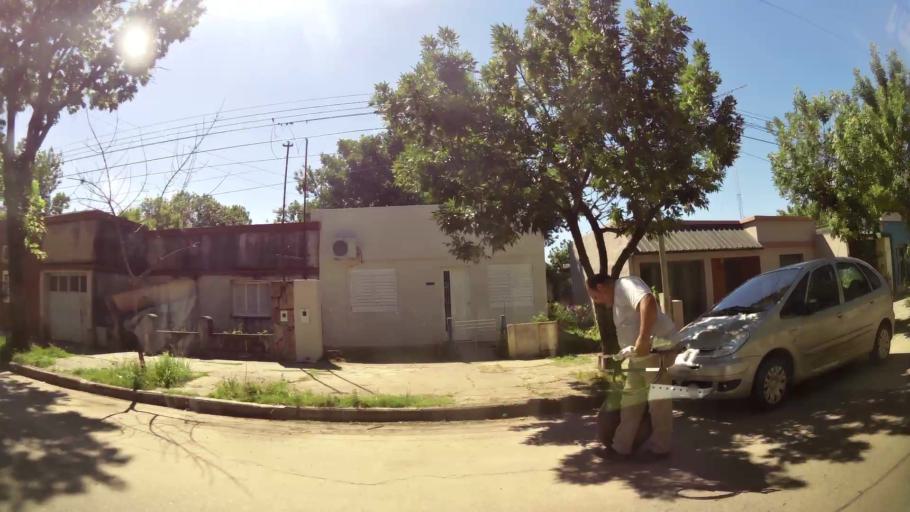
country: AR
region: Santa Fe
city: Esperanza
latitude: -31.4384
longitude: -60.9261
